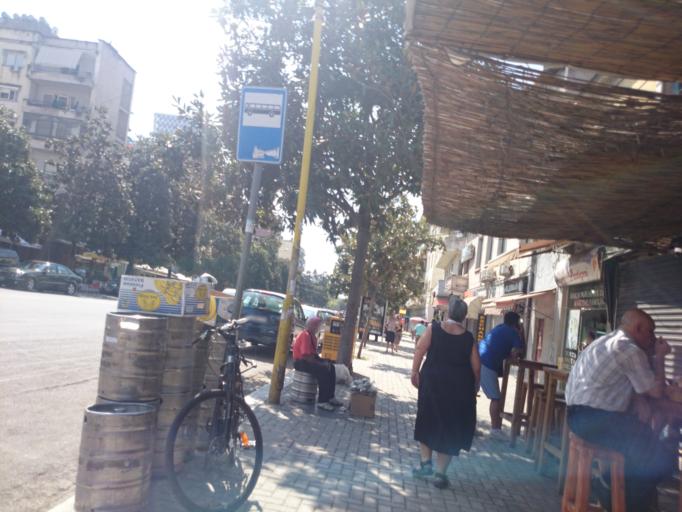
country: AL
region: Tirane
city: Tirana
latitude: 41.3292
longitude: 19.8244
